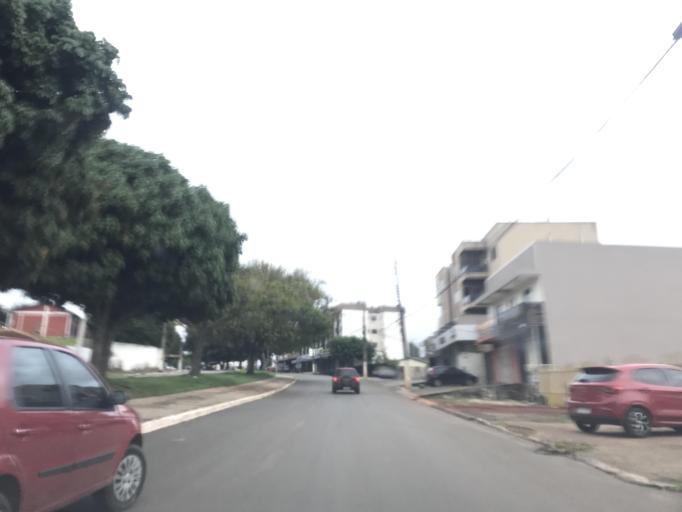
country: BR
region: Goias
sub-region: Luziania
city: Luziania
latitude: -16.2598
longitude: -47.9580
